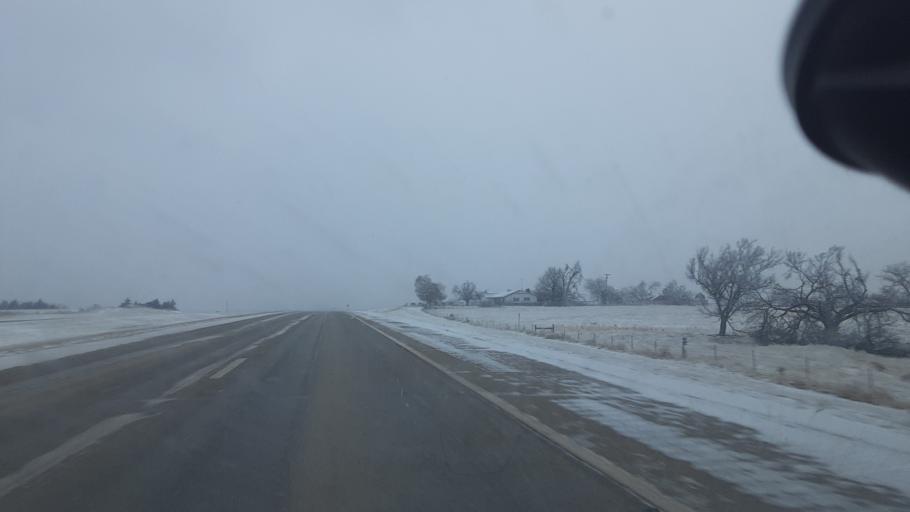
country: US
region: Oklahoma
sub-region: Logan County
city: Guthrie
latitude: 35.9008
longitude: -97.3496
